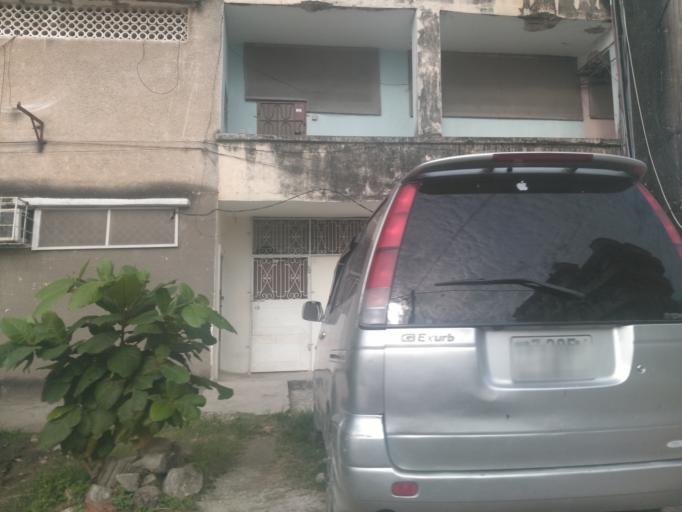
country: TZ
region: Zanzibar Urban/West
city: Zanzibar
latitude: -6.1628
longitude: 39.1993
